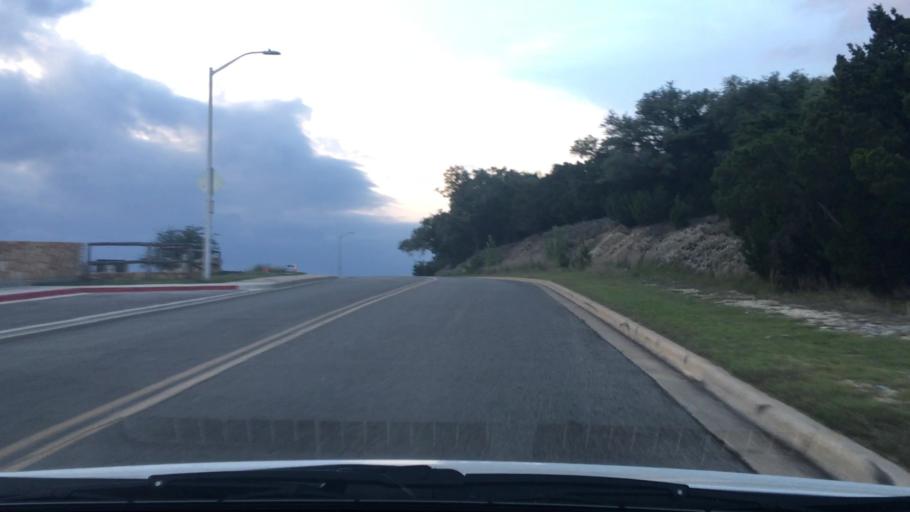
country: US
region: Texas
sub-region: Williamson County
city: Anderson Mill
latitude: 30.4518
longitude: -97.8585
